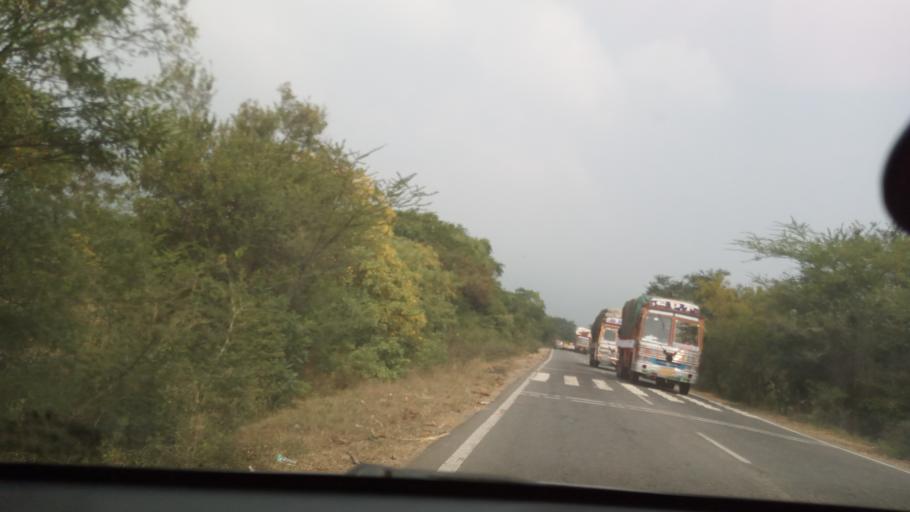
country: IN
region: Tamil Nadu
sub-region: Erode
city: Sathyamangalam
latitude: 11.5635
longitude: 77.1353
